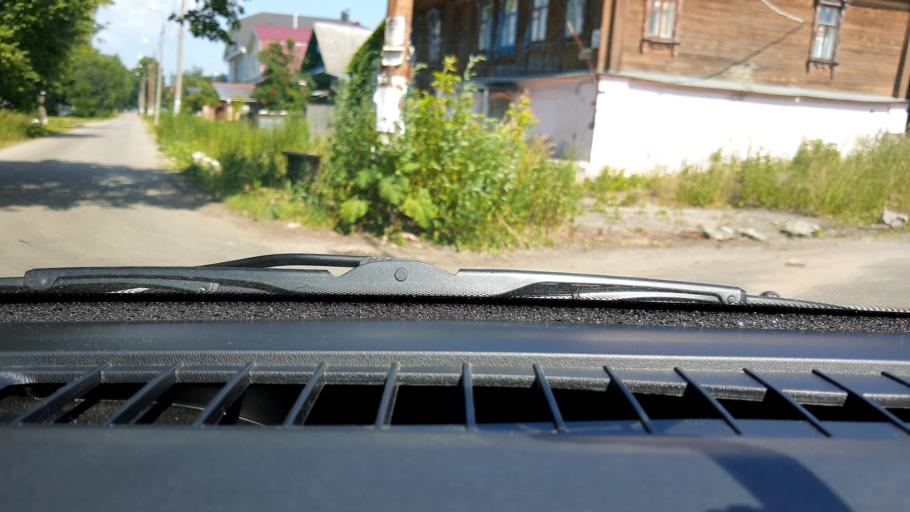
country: RU
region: Nizjnij Novgorod
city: Gorbatovka
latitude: 56.2028
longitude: 43.7648
